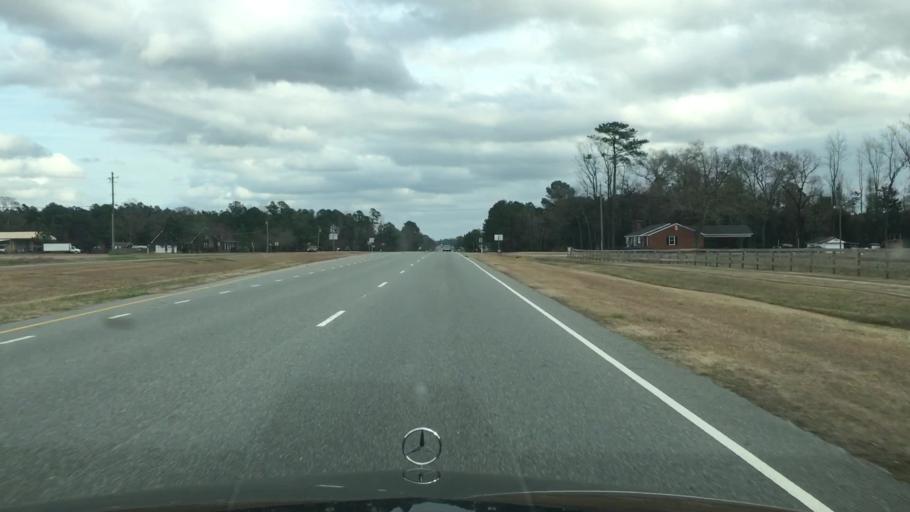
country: US
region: North Carolina
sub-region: Duplin County
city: Beulaville
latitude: 34.9300
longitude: -77.8149
